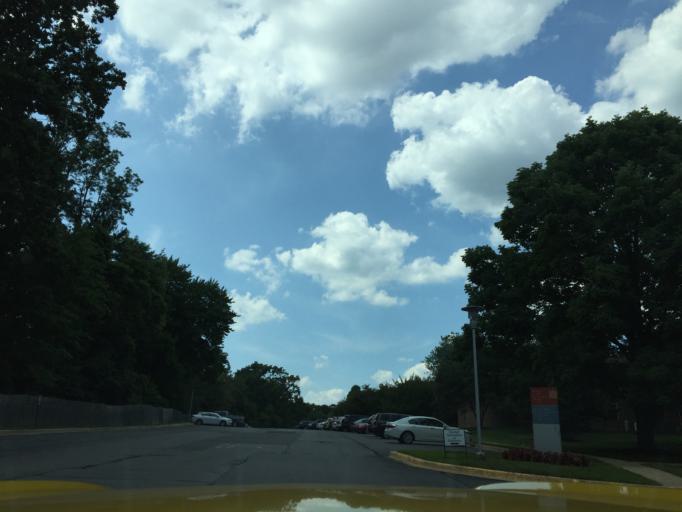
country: US
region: Delaware
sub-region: New Castle County
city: Bellefonte
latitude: 39.8004
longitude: -75.5253
